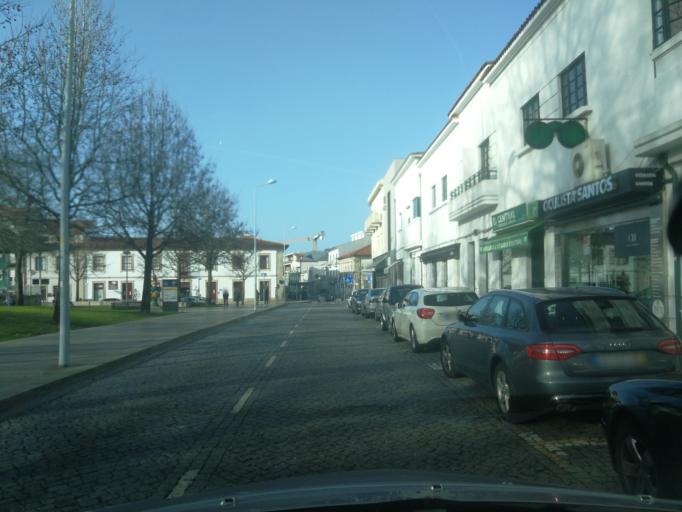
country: PT
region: Braga
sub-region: Barcelos
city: Barcelos
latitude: 41.5339
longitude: -8.6193
